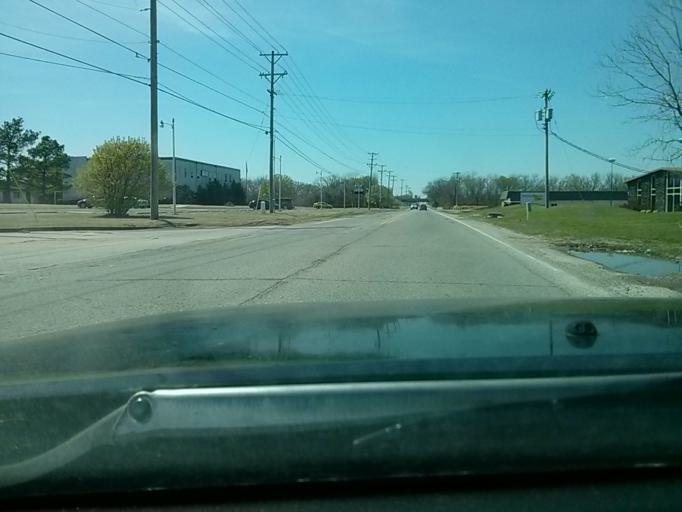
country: US
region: Oklahoma
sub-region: Tulsa County
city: Owasso
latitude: 36.1770
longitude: -95.8776
